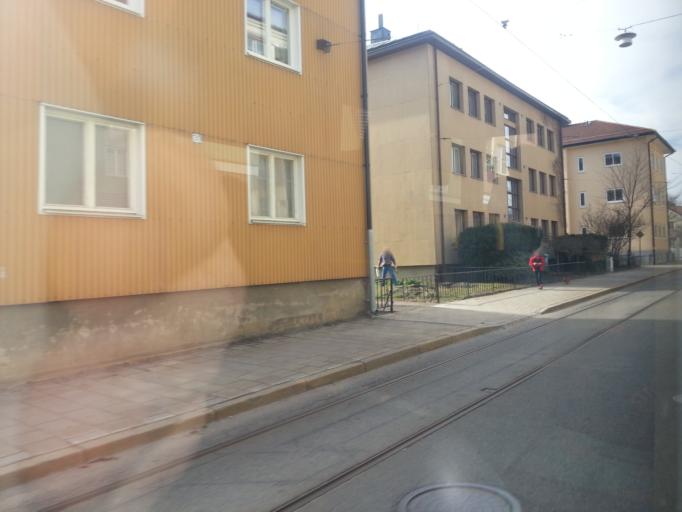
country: SE
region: OEstergoetland
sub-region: Norrkopings Kommun
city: Norrkoping
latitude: 58.5864
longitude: 16.1761
